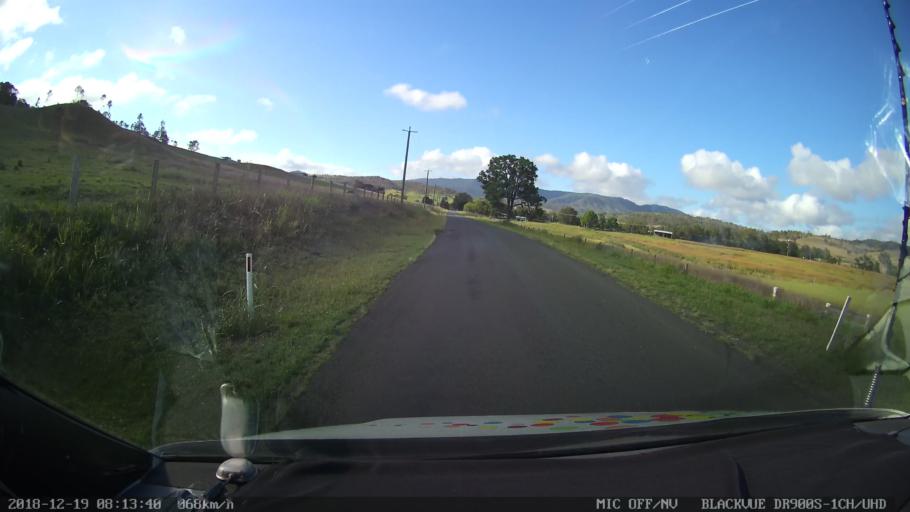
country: AU
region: Queensland
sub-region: Logan
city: Cedar Vale
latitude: -28.2408
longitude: 152.8903
